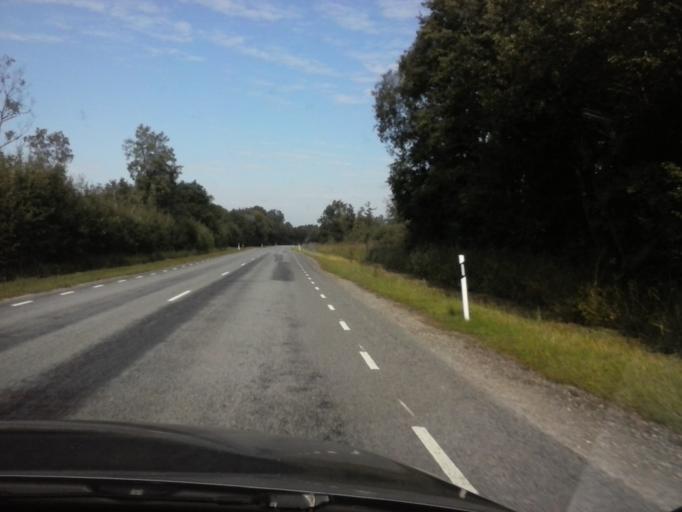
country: EE
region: Laeaene
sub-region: Ridala Parish
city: Uuemoisa
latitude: 58.8375
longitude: 23.6596
